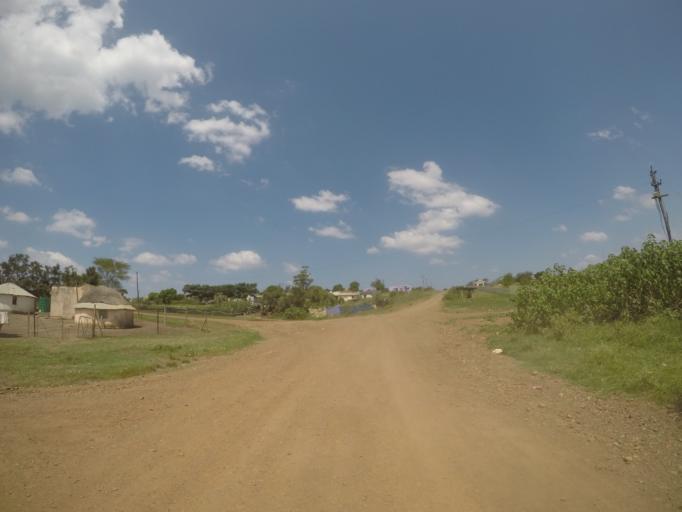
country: ZA
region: KwaZulu-Natal
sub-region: uThungulu District Municipality
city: Empangeni
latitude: -28.5891
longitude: 31.7407
